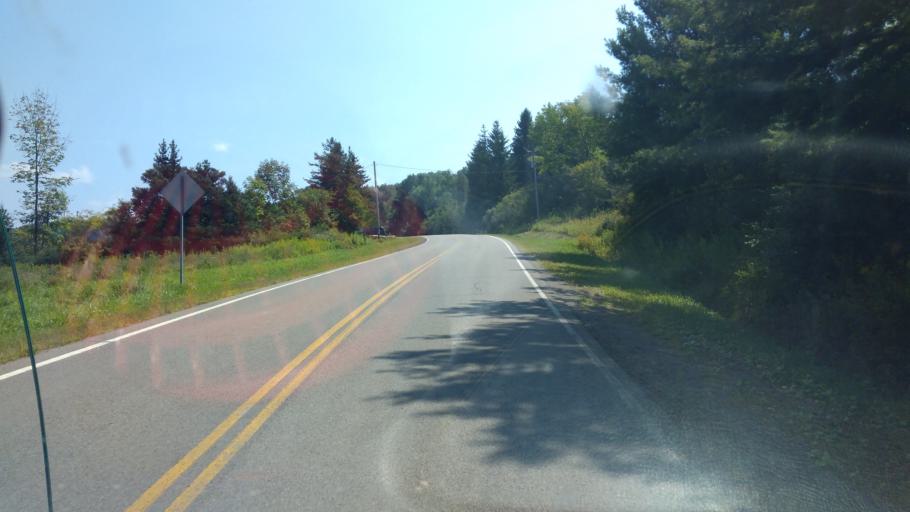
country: US
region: New York
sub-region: Allegany County
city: Belmont
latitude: 42.2913
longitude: -77.9367
